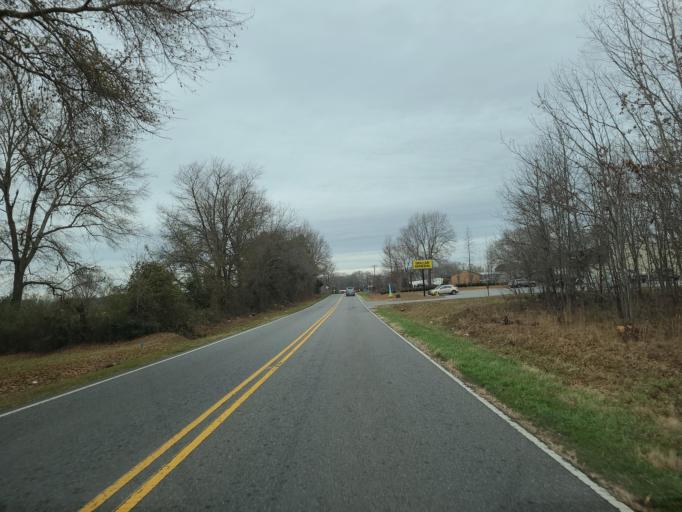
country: US
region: North Carolina
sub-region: Cleveland County
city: Shelby
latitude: 35.3600
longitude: -81.5734
